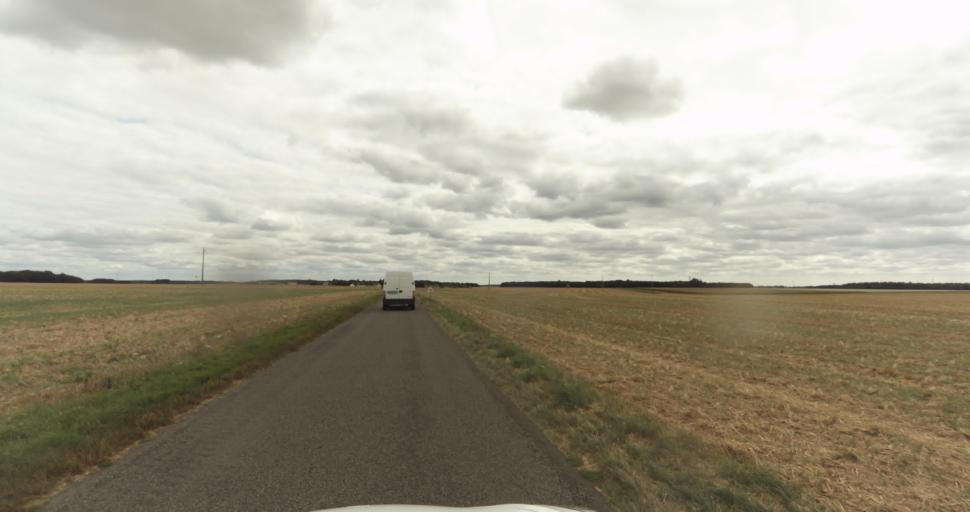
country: FR
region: Centre
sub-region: Departement d'Eure-et-Loir
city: Saint-Remy-sur-Avre
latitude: 48.8069
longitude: 1.2499
